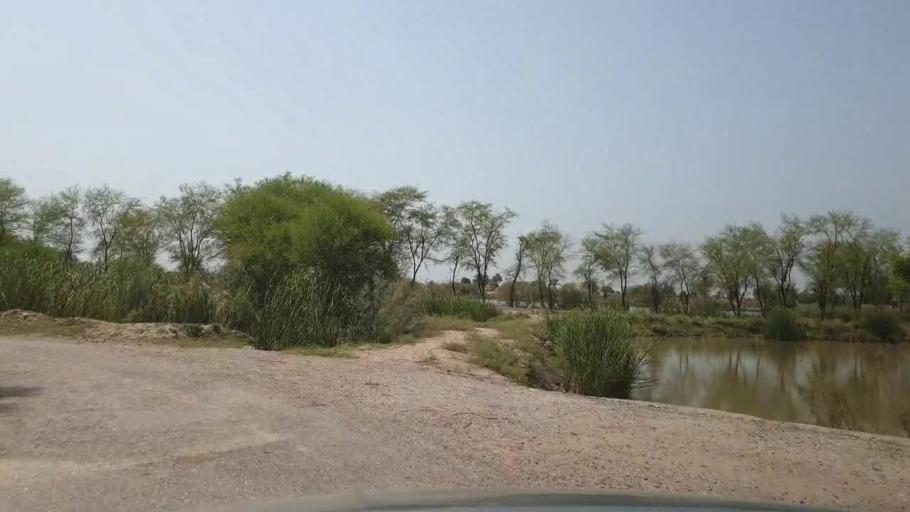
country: PK
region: Sindh
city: Garhi Yasin
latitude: 27.8944
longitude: 68.4518
